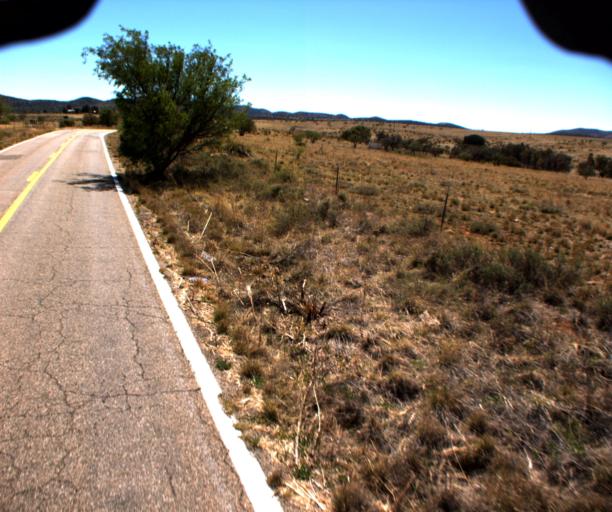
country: US
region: Arizona
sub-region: Cochise County
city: Huachuca City
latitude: 31.5895
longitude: -110.5610
